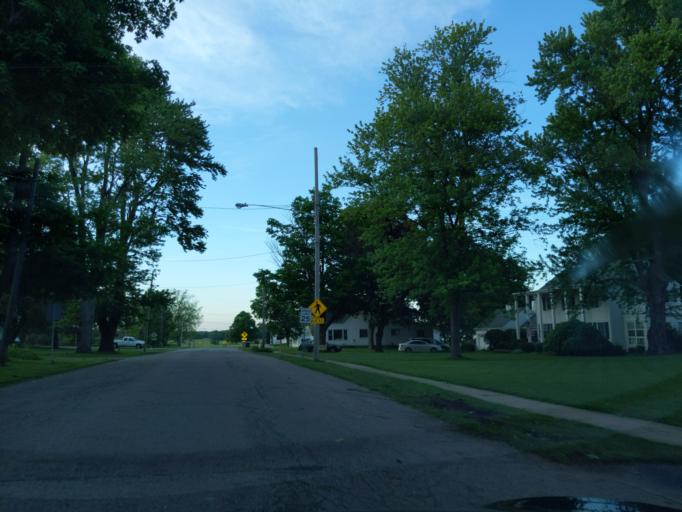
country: US
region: Michigan
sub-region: Ingham County
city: Williamston
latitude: 42.5574
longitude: -84.3030
